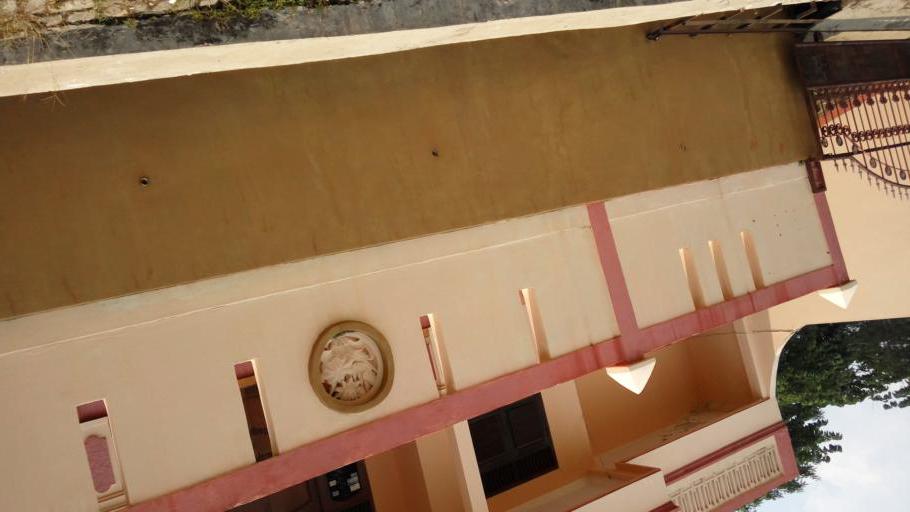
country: ID
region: Central Java
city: Mranggen
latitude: -7.0421
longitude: 110.4741
